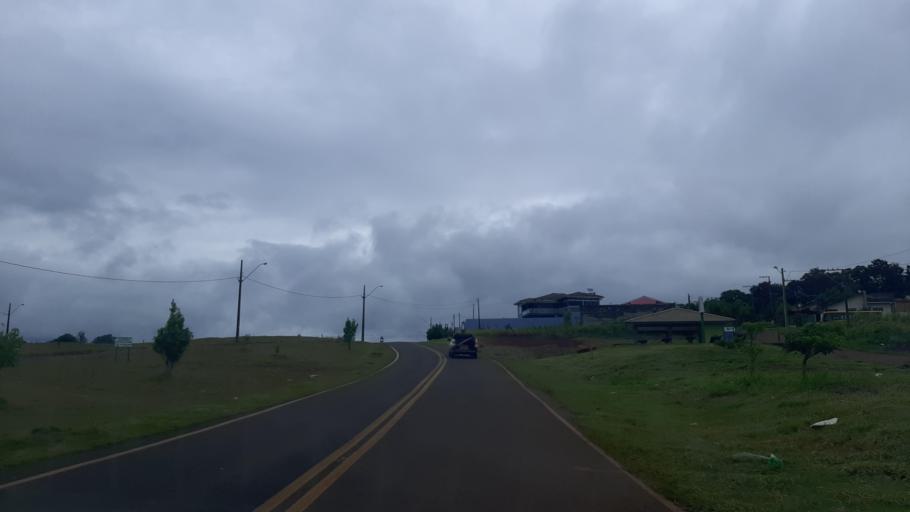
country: BR
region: Parana
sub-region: Ampere
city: Ampere
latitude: -25.9295
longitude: -53.4665
